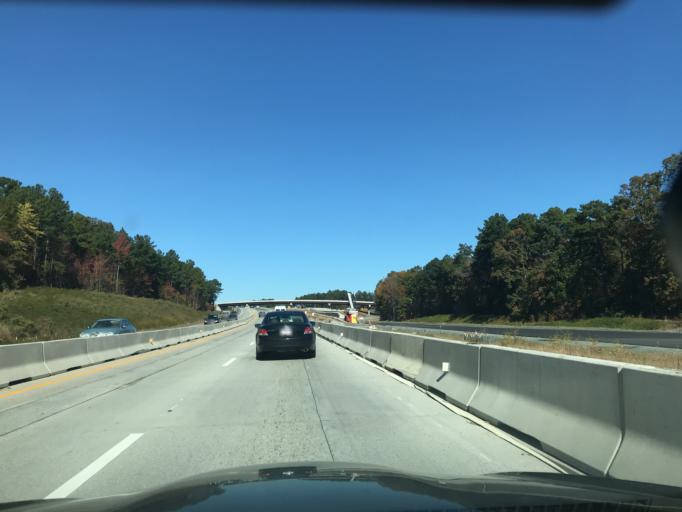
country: US
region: North Carolina
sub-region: Durham County
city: Durham
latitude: 35.9604
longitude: -78.8648
